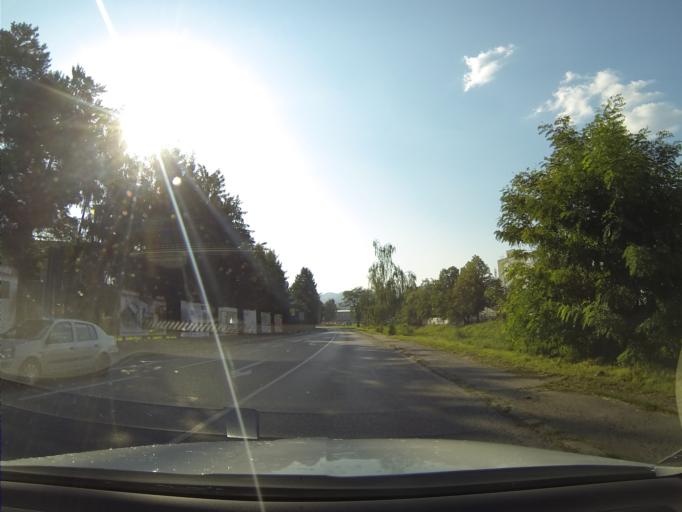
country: SK
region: Nitriansky
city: Prievidza
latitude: 48.7694
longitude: 18.6201
